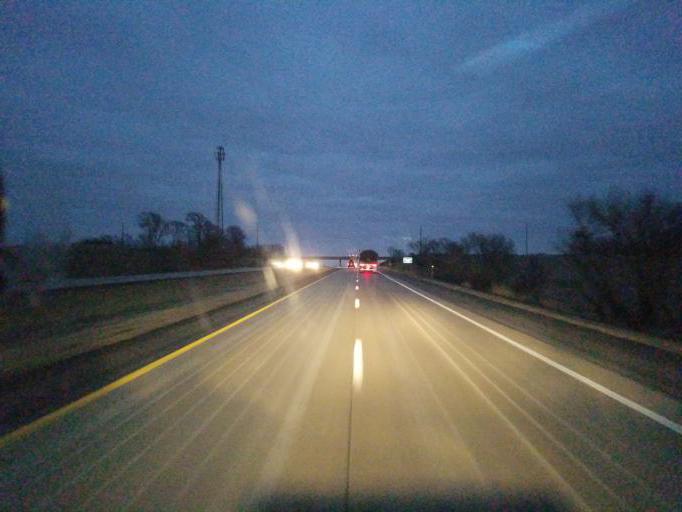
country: US
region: Iowa
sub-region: Cass County
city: Atlantic
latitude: 41.4962
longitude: -94.7814
